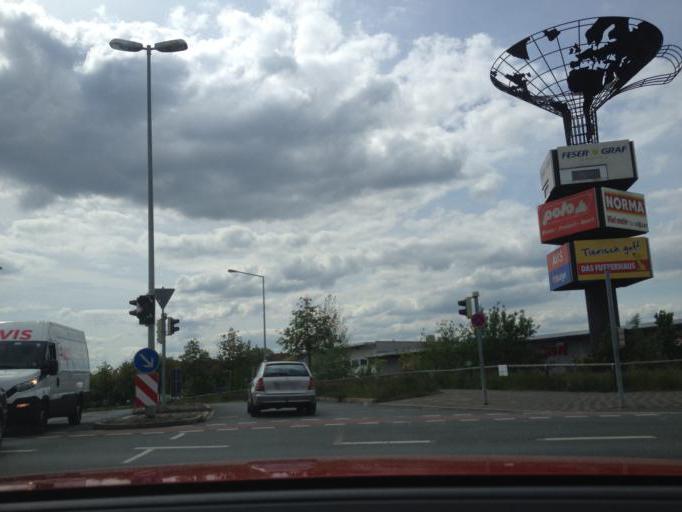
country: DE
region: Bavaria
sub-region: Regierungsbezirk Mittelfranken
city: Grossreuth bei Schweinau
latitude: 49.4343
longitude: 11.0383
